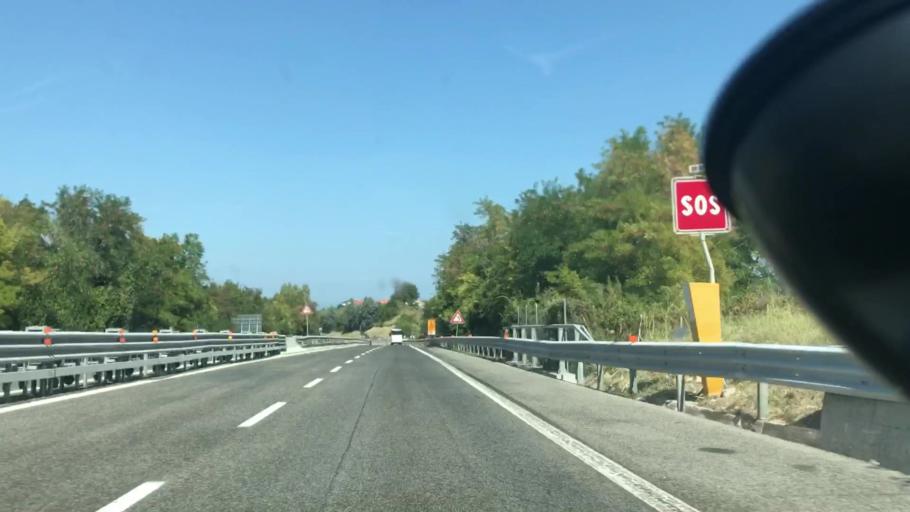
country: IT
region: Abruzzo
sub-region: Provincia di Chieti
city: San Vito Chietino
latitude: 42.3063
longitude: 14.4221
